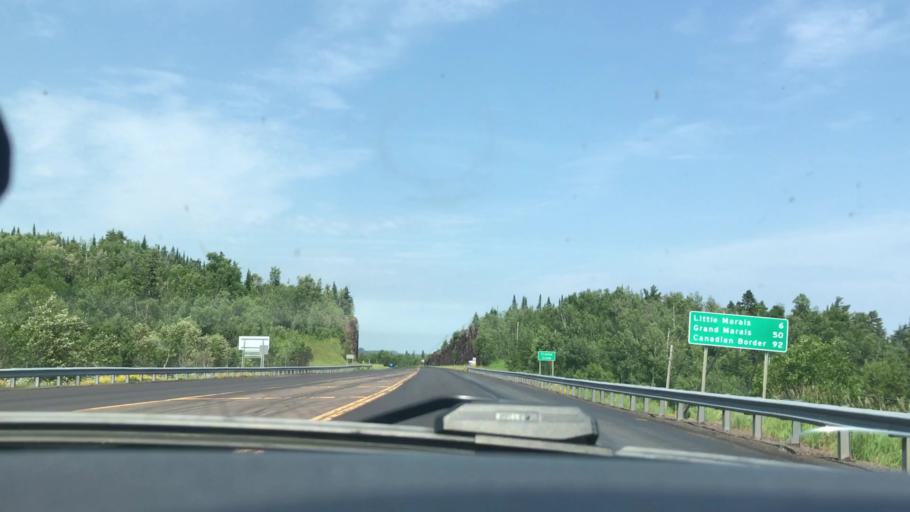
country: US
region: Minnesota
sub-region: Lake County
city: Silver Bay
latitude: 47.3472
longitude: -91.1869
